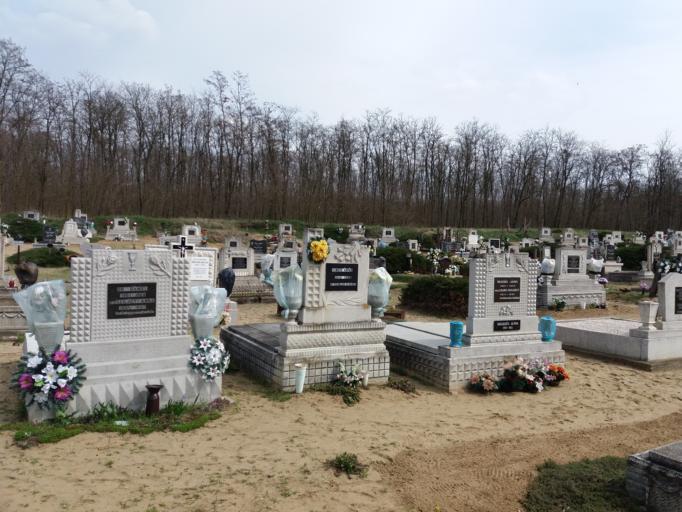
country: HU
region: Szabolcs-Szatmar-Bereg
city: Petnehaza
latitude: 48.0508
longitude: 22.0455
